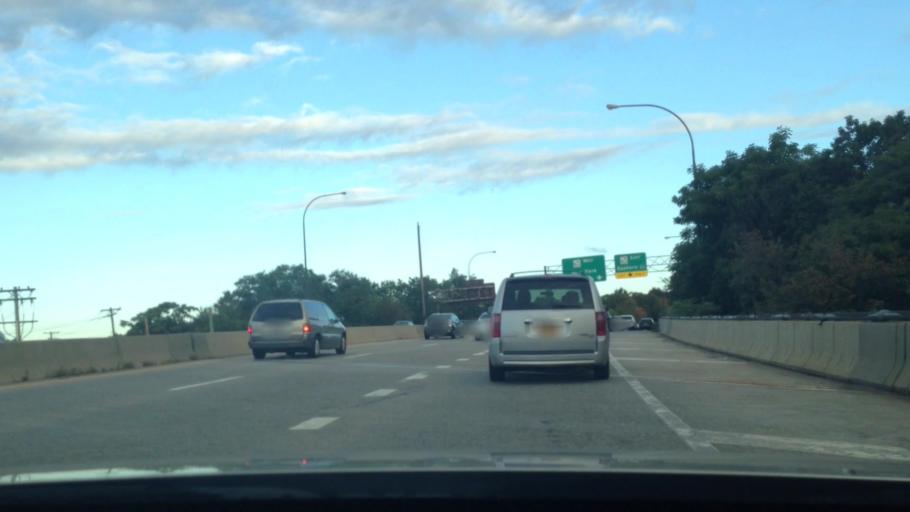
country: US
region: New York
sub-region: Nassau County
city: Carle Place
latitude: 40.7487
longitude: -73.6150
